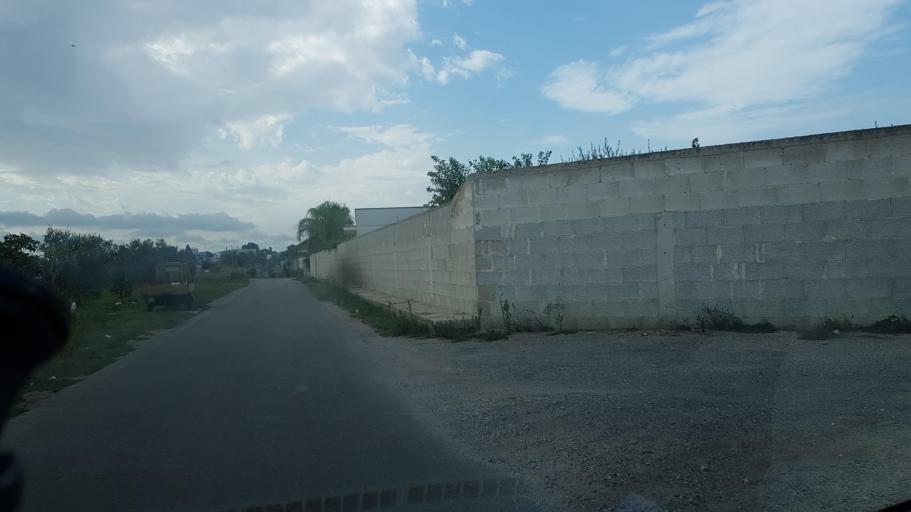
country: IT
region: Apulia
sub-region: Provincia di Brindisi
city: San Pietro Vernotico
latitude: 40.4935
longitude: 18.0043
